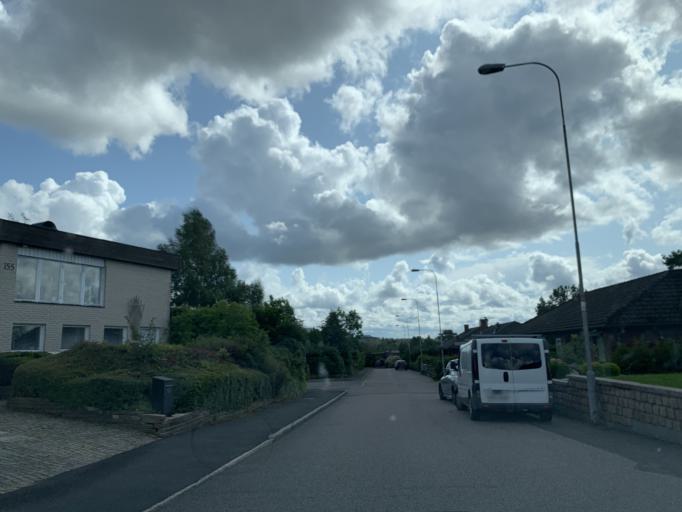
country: SE
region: Vaestra Goetaland
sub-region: Goteborg
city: Hammarkullen
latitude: 57.7761
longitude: 12.0261
